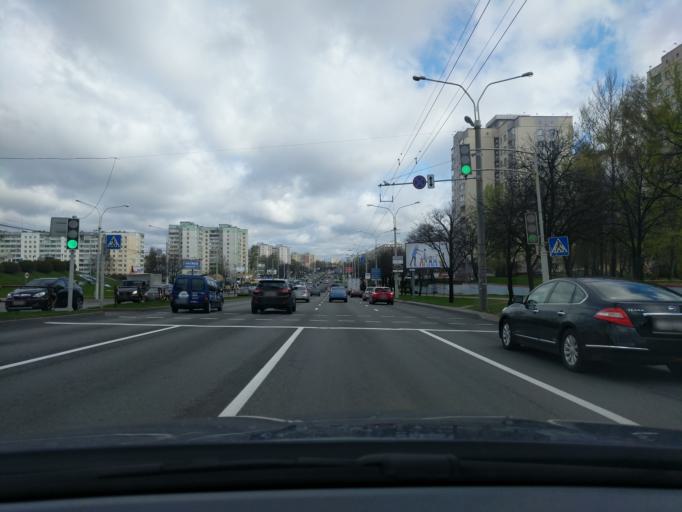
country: BY
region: Minsk
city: Novoye Medvezhino
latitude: 53.9073
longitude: 27.4960
